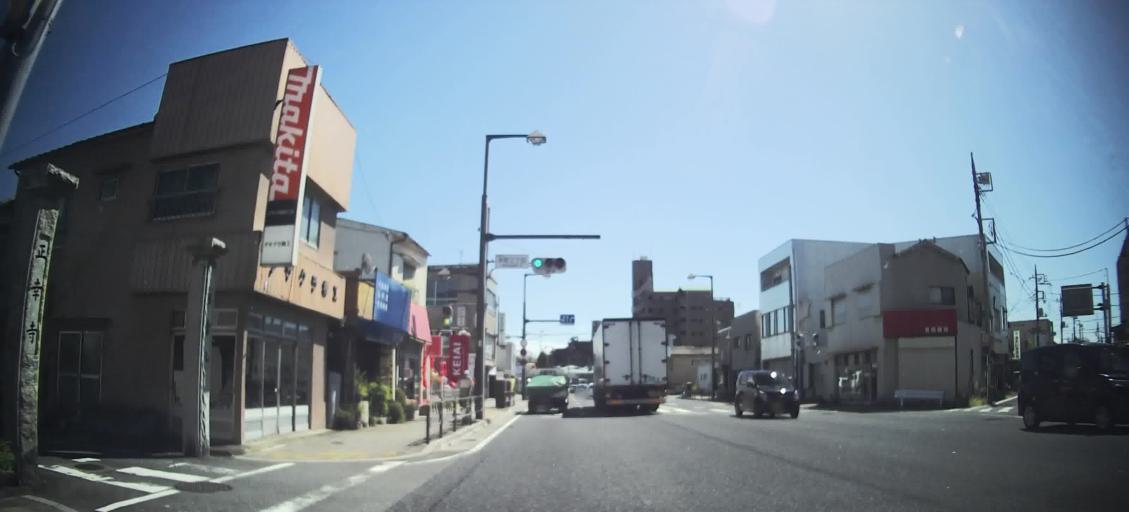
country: JP
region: Gunma
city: Maebashi-shi
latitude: 36.3865
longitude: 139.0759
